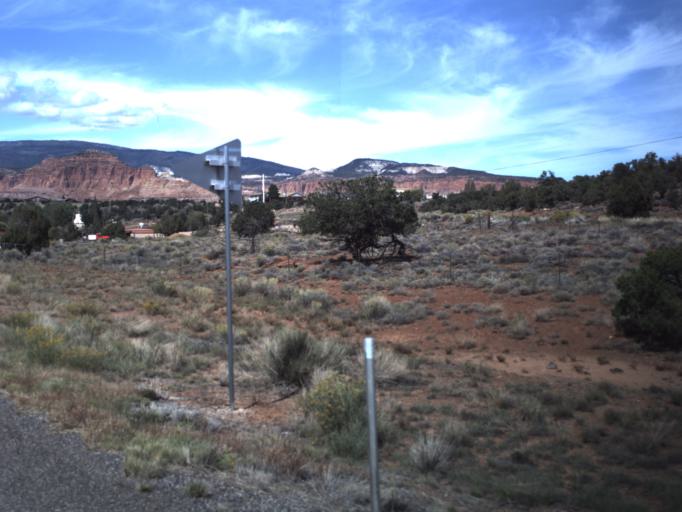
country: US
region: Utah
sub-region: Wayne County
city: Loa
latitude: 38.2943
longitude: -111.3988
